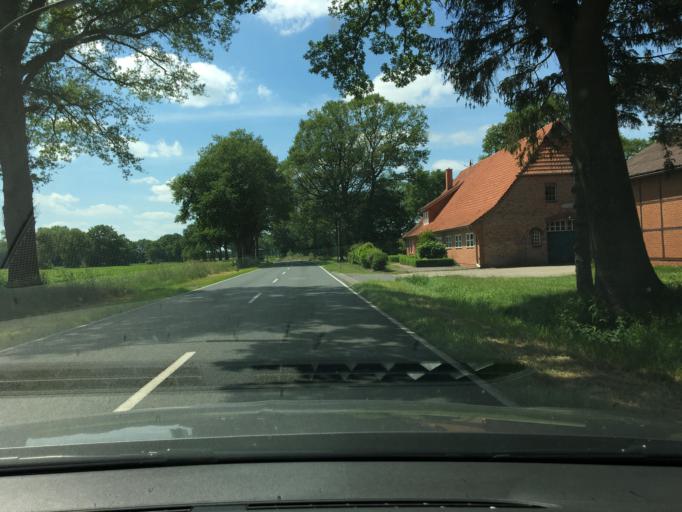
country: DE
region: Lower Saxony
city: Zeven
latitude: 53.2562
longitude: 9.2479
